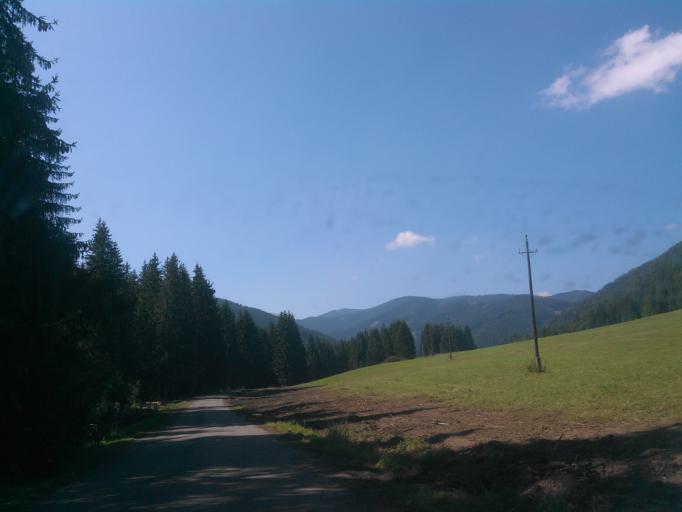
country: SK
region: Zilinsky
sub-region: Okres Liptovsky Mikulas
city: Liptovsky Mikulas
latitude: 49.0110
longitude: 19.5184
